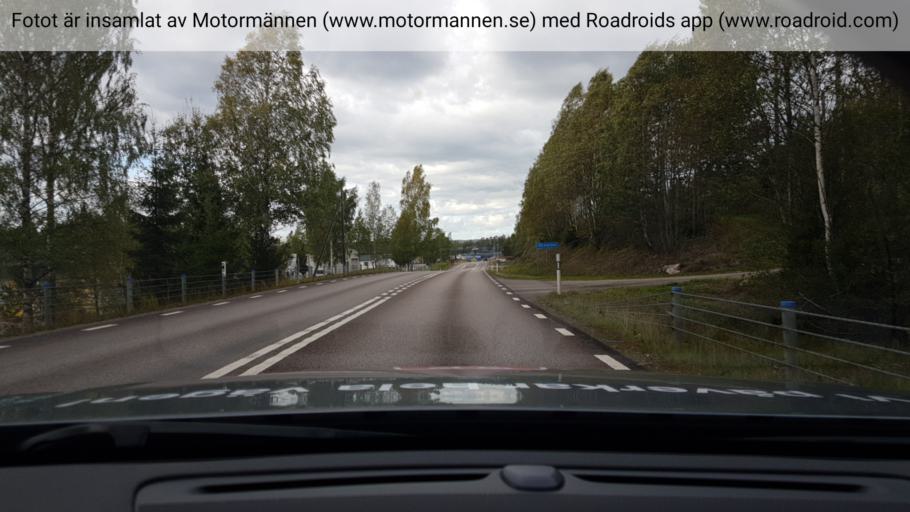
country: SE
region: Vaermland
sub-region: Arjangs Kommun
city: Toecksfors
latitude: 59.5043
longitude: 11.8660
